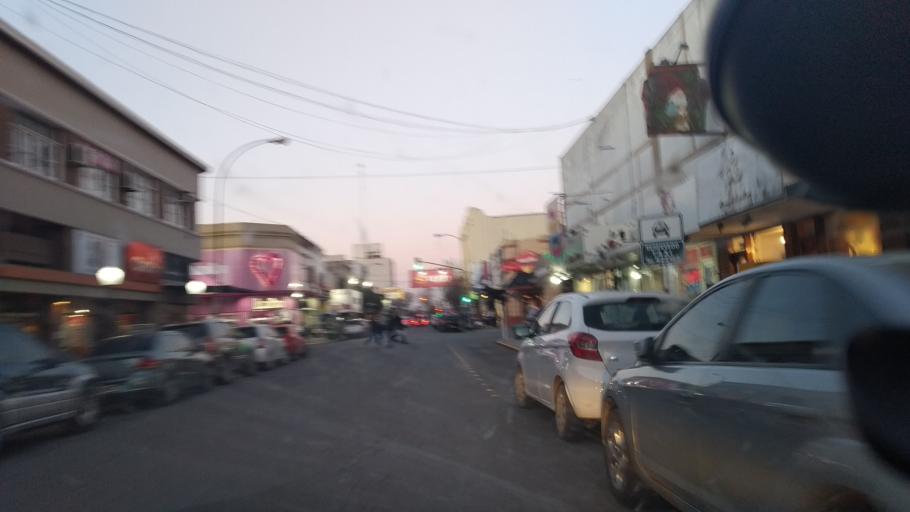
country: AR
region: Buenos Aires
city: Necochea
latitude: -38.5541
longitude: -58.7427
